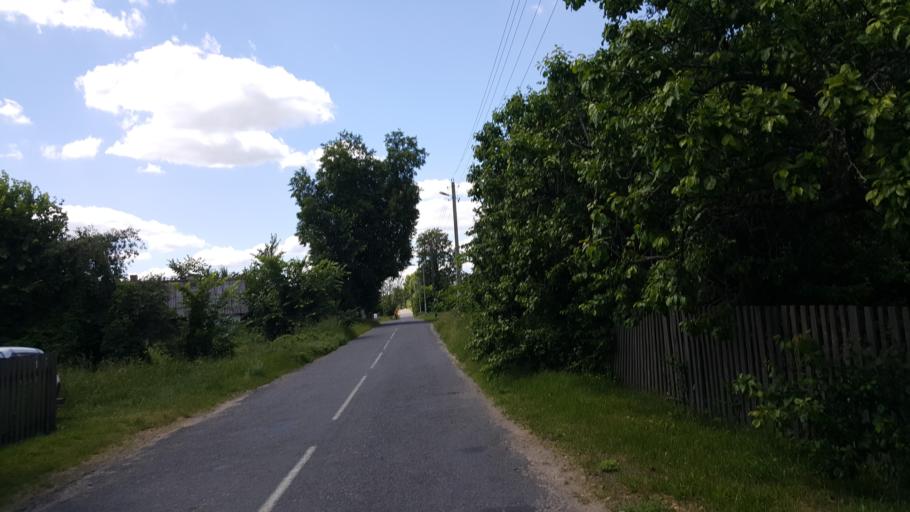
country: PL
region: Podlasie
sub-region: Powiat hajnowski
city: Czeremcha
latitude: 52.5127
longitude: 23.5462
